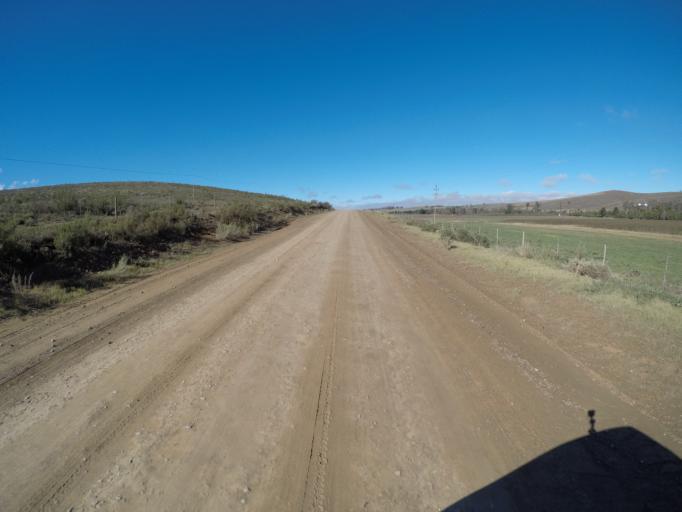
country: ZA
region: Western Cape
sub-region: Overberg District Municipality
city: Caledon
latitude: -34.0894
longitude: 19.6595
